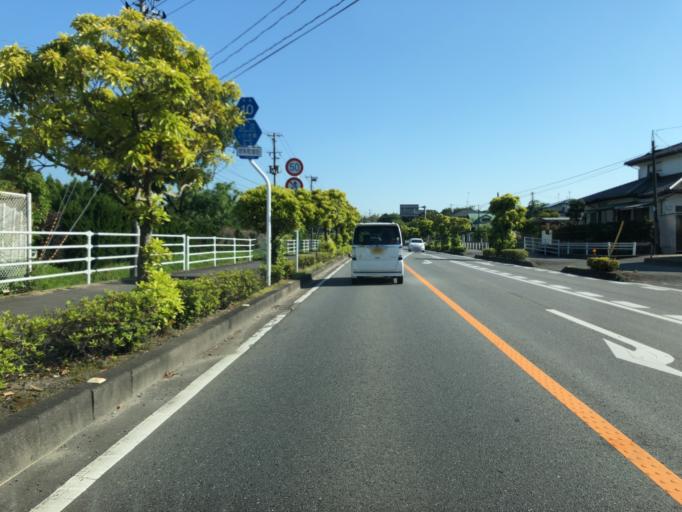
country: JP
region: Ibaraki
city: Kitaibaraki
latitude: 36.8991
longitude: 140.7674
